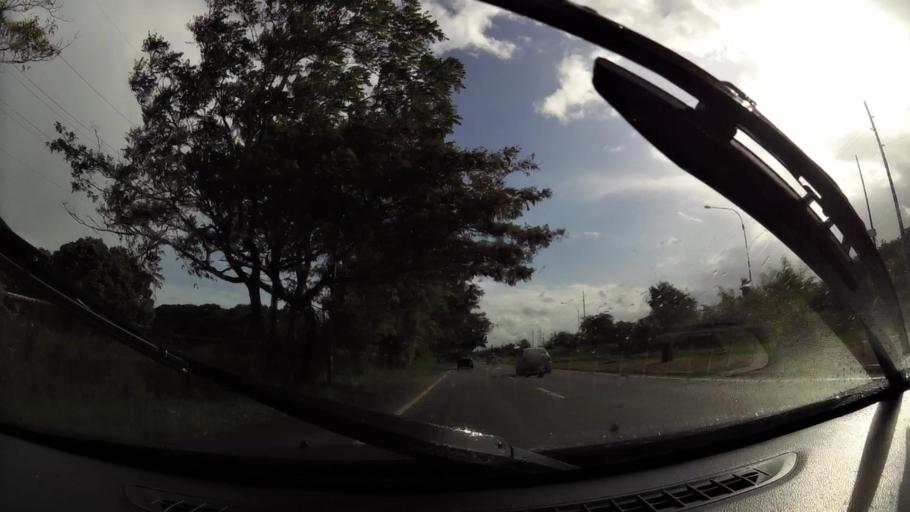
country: TT
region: Tunapuna/Piarco
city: Tunapuna
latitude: 10.6402
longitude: -61.4311
